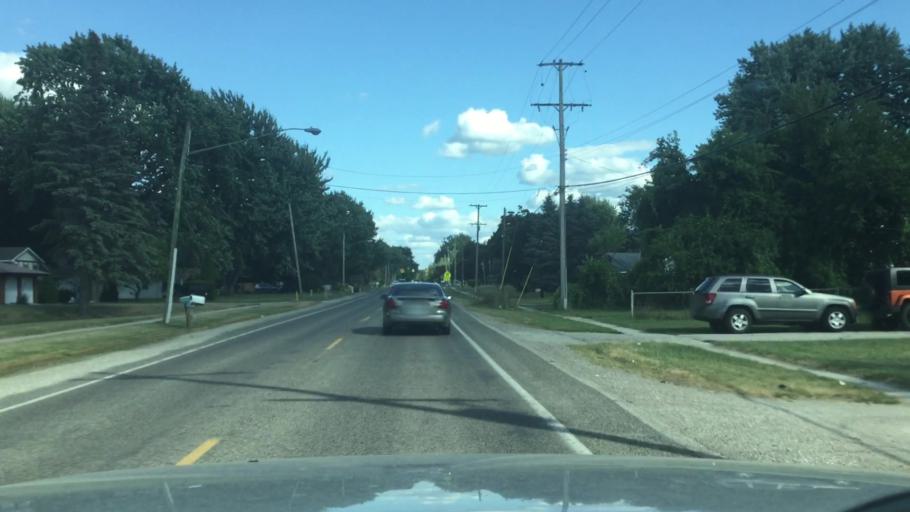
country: US
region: Michigan
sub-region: Saginaw County
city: Bridgeport
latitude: 43.3728
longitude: -83.9065
